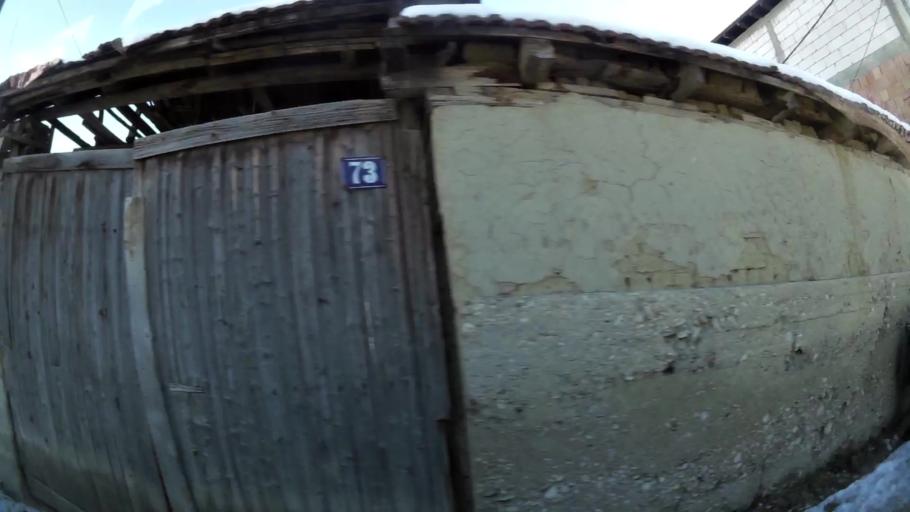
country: MK
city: Grchec
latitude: 41.9904
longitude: 21.3303
